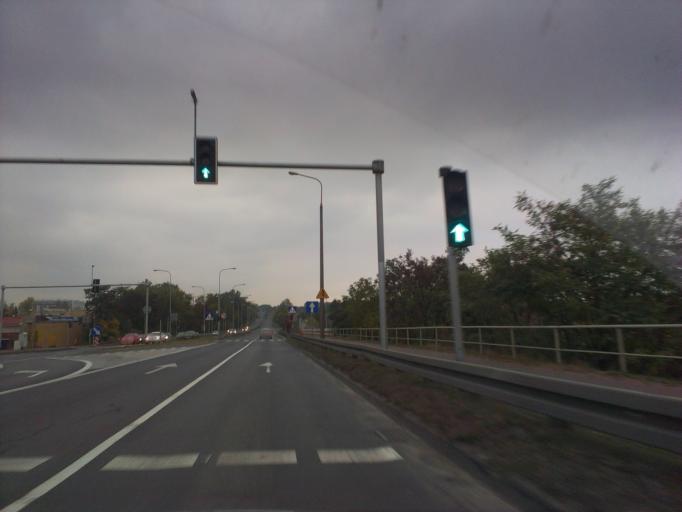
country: PL
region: Greater Poland Voivodeship
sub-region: Powiat poznanski
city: Czerwonak
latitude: 52.4306
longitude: 16.9618
